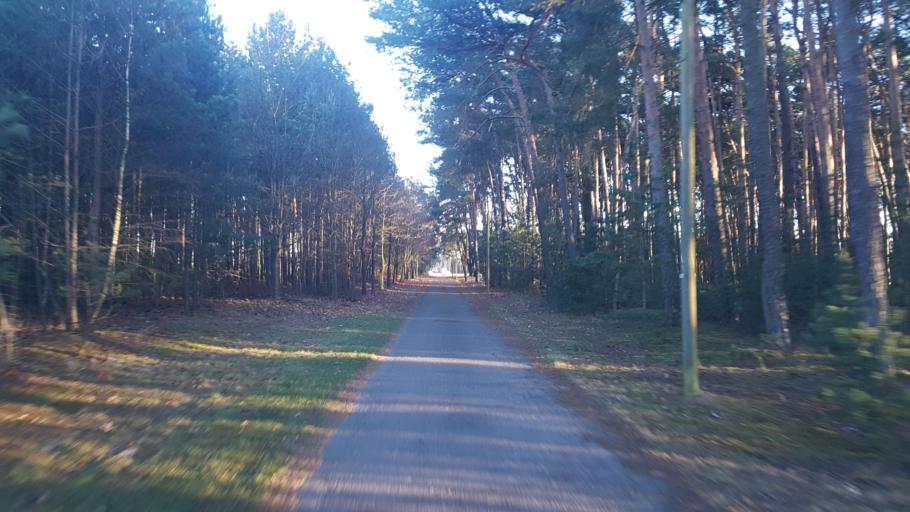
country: DE
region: Brandenburg
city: Peitz
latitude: 51.8877
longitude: 14.3947
